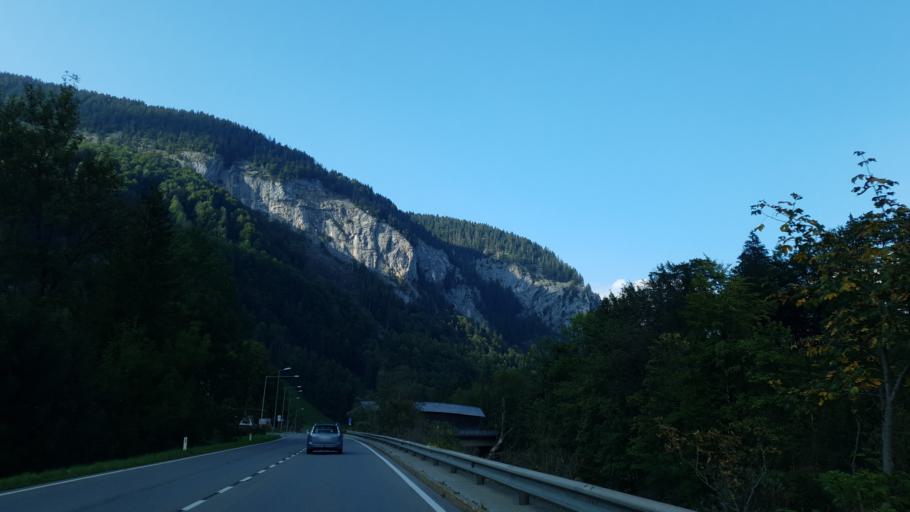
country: AT
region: Vorarlberg
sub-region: Politischer Bezirk Bregenz
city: Reuthe
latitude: 47.3608
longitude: 9.8789
